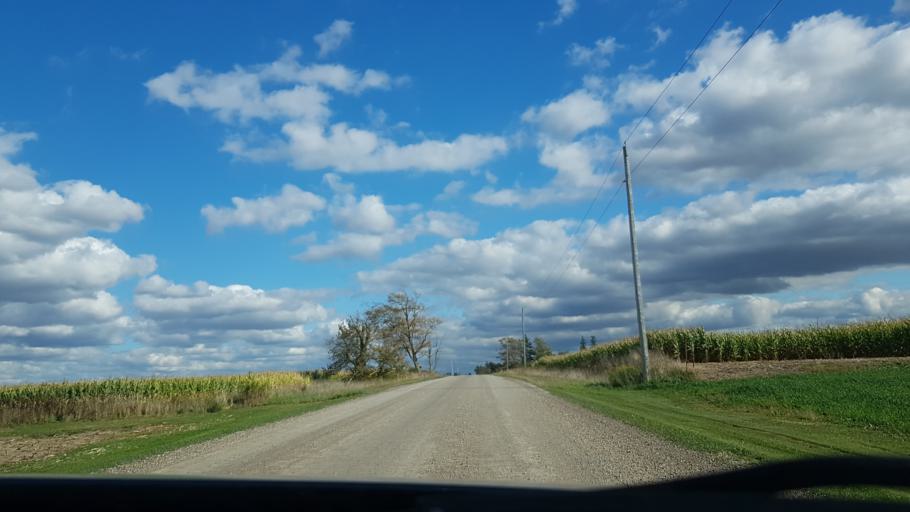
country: CA
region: Ontario
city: South Huron
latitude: 43.1137
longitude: -81.6544
